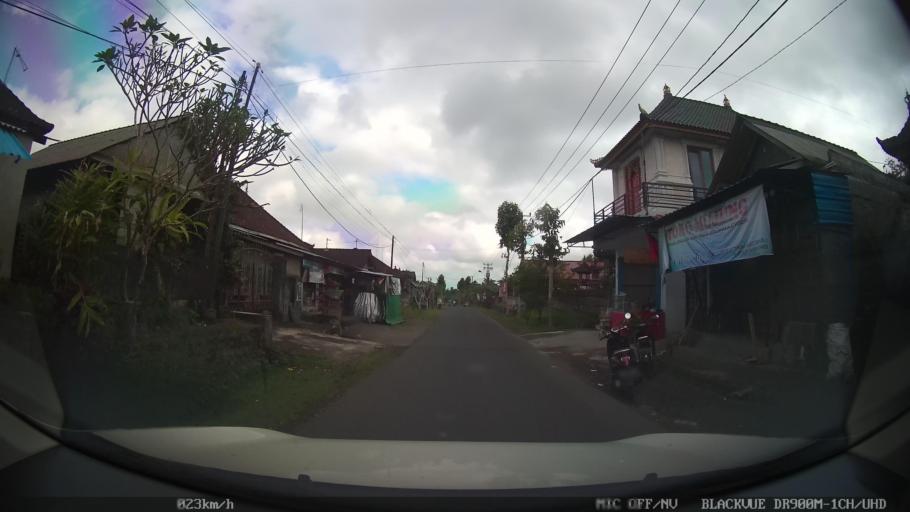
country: ID
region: Bali
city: Banjar Susut Kaja
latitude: -8.4366
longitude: 115.3222
